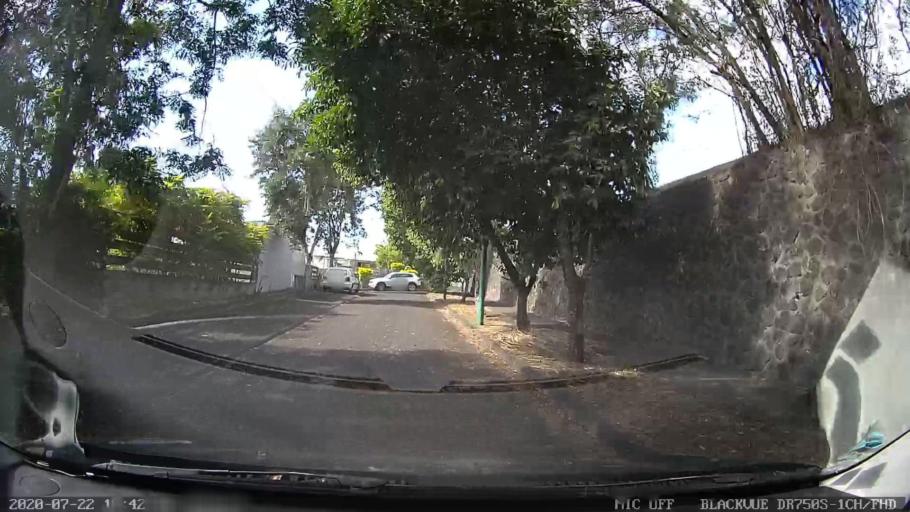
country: RE
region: Reunion
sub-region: Reunion
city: Sainte-Suzanne
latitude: -20.9035
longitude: 55.5979
